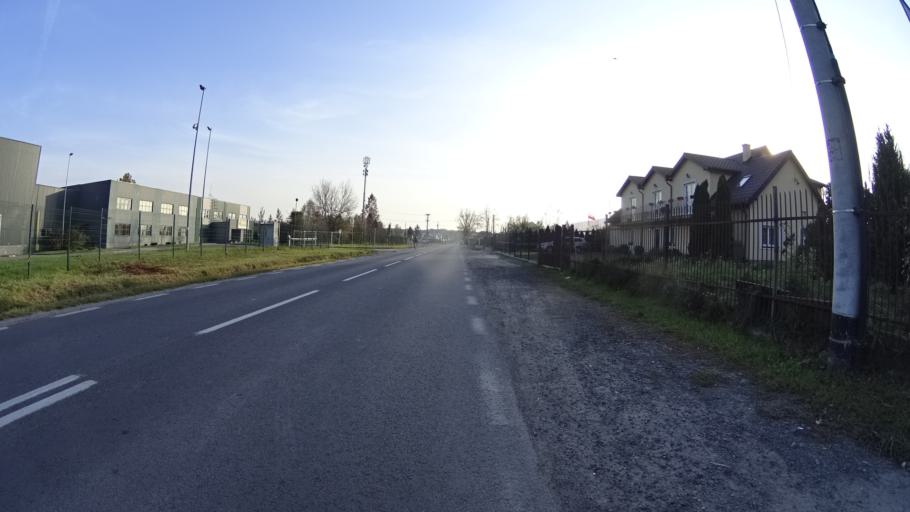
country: PL
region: Masovian Voivodeship
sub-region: Powiat warszawski zachodni
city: Babice
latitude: 52.2832
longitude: 20.8670
